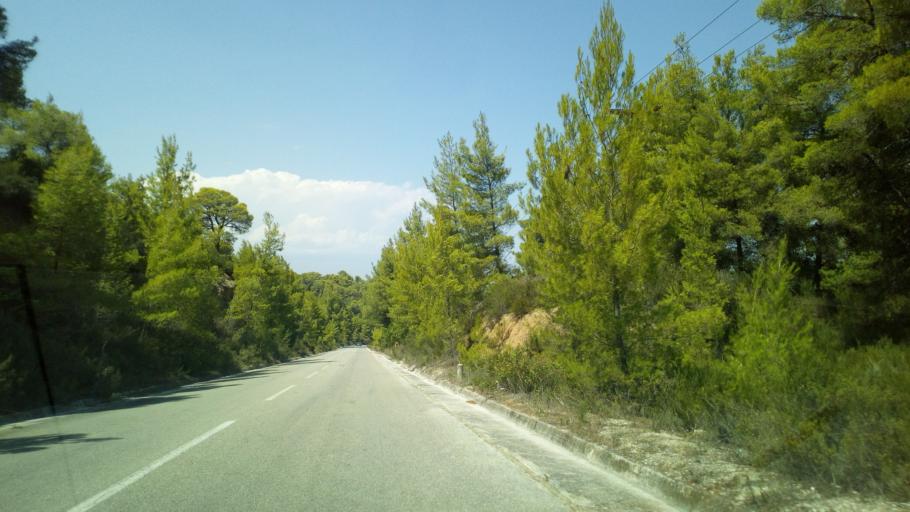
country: GR
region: Central Macedonia
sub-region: Nomos Chalkidikis
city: Sarti
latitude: 40.1442
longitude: 23.9211
